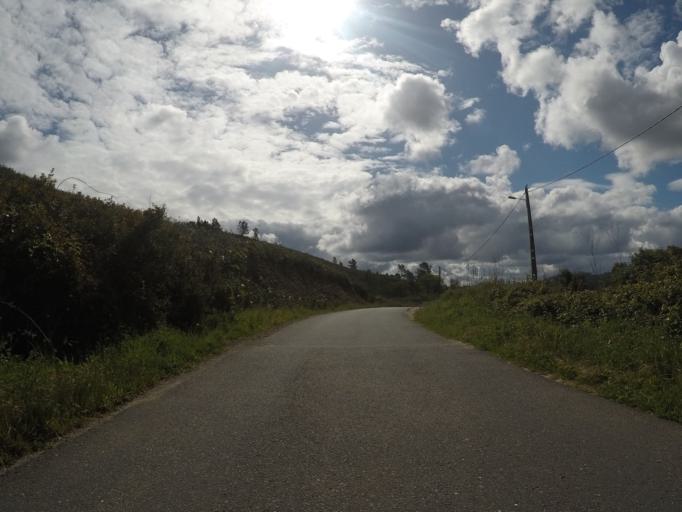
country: PT
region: Beja
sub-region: Odemira
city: Sao Teotonio
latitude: 37.4362
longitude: -8.7657
